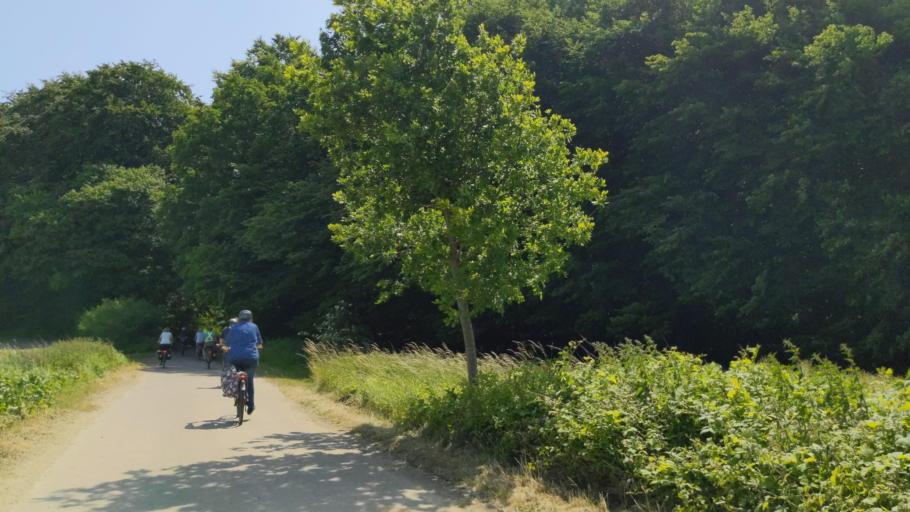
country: DE
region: Schleswig-Holstein
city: Behlendorf
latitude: 53.6918
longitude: 10.6831
